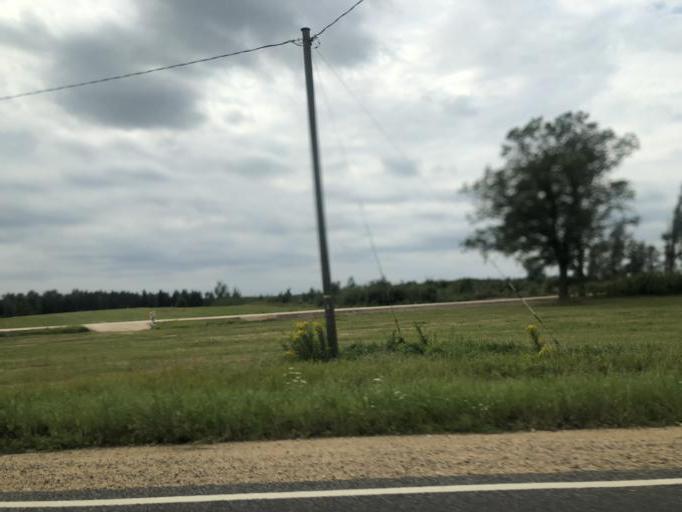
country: LV
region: Baldone
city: Baldone
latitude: 56.6928
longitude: 24.3881
